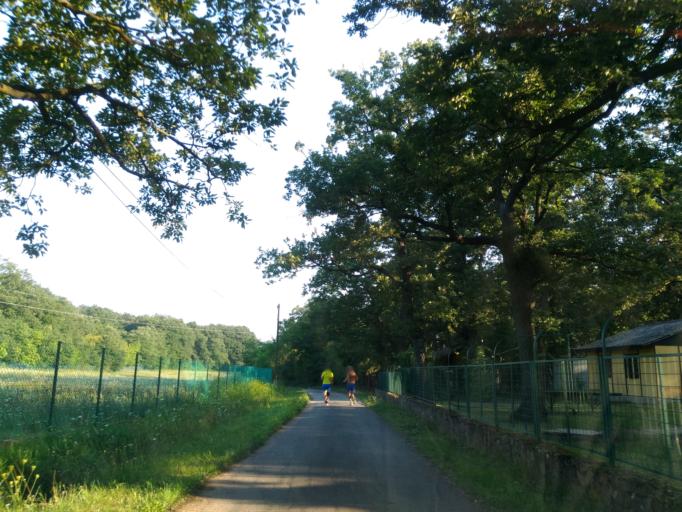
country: HU
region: Veszprem
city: Zanka
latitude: 46.8631
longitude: 17.6676
